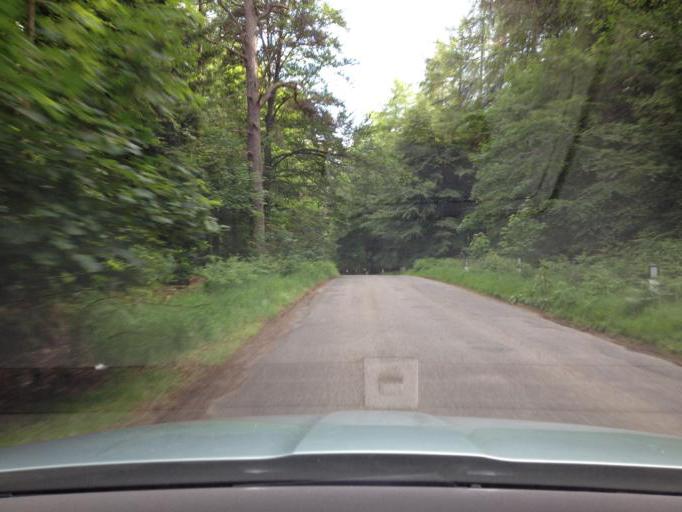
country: GB
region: Scotland
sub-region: Aberdeenshire
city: Banchory
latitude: 56.9715
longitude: -2.5788
